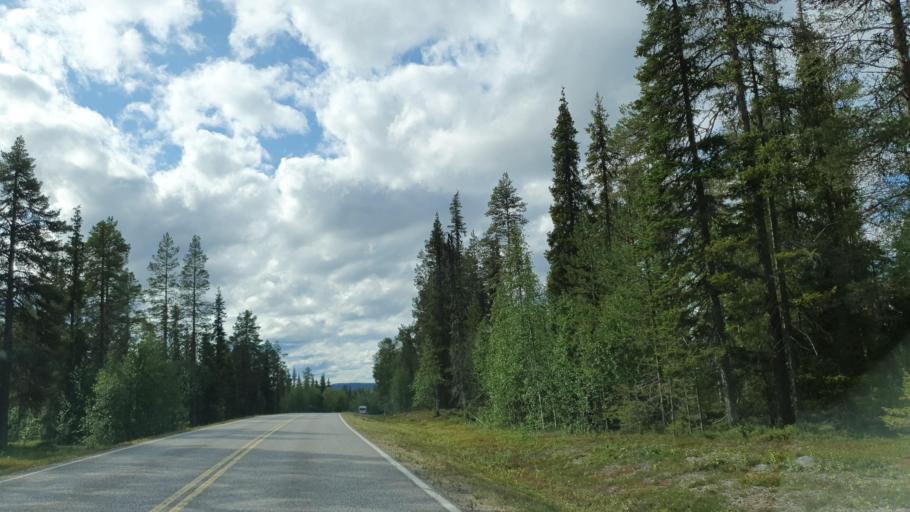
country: FI
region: Lapland
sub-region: Tunturi-Lappi
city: Muonio
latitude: 67.8730
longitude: 24.1964
